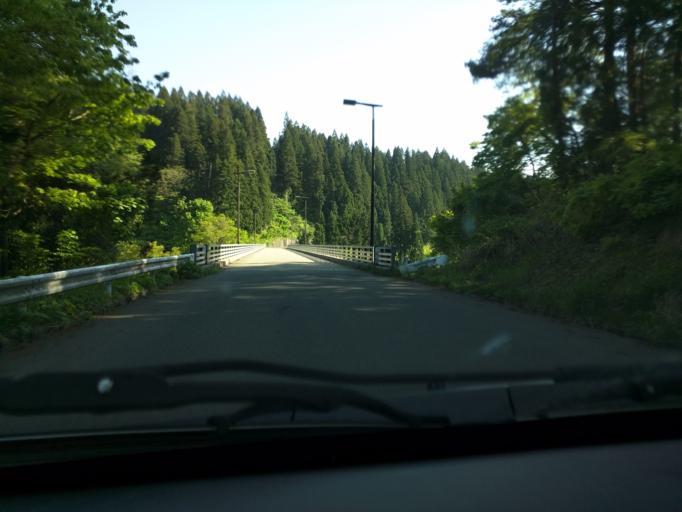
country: JP
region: Fukushima
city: Kitakata
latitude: 37.4799
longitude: 139.6696
